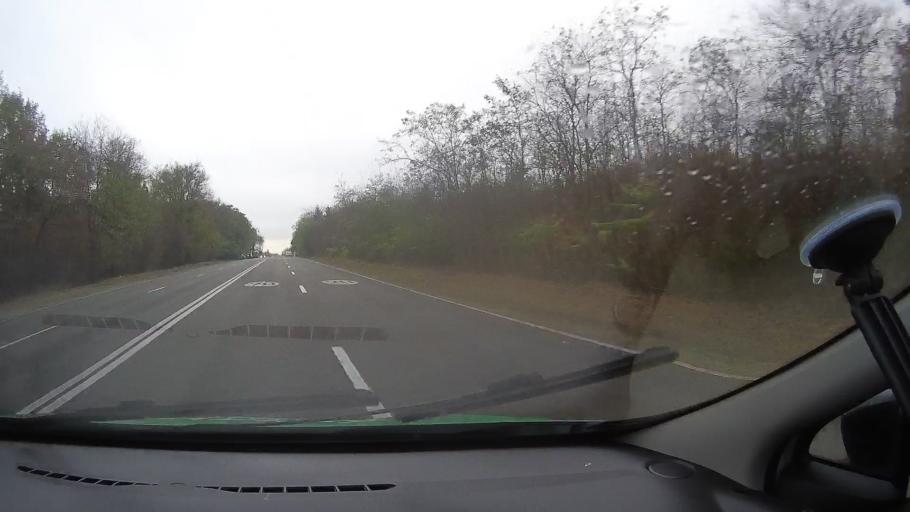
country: RO
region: Constanta
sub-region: Comuna Valu lui Traian
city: Valu lui Traian
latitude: 44.1650
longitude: 28.4935
